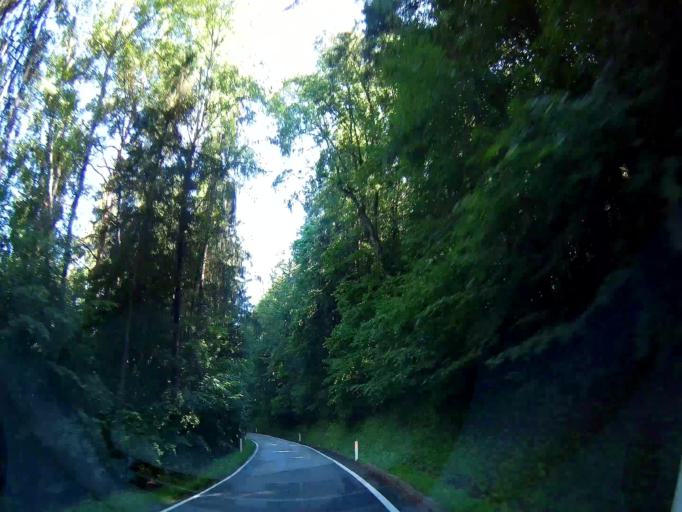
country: AT
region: Carinthia
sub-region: Politischer Bezirk Volkermarkt
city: Diex
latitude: 46.6939
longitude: 14.5801
